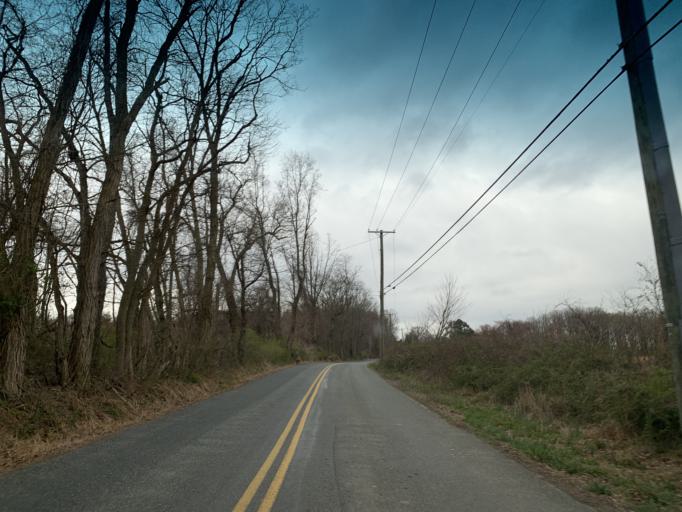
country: US
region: Maryland
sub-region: Harford County
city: Aberdeen
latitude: 39.5372
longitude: -76.2014
